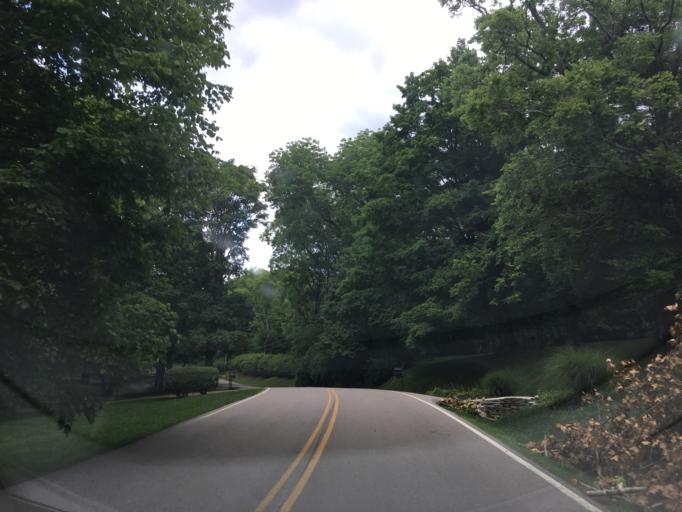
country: US
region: Tennessee
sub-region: Davidson County
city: Forest Hills
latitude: 36.0880
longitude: -86.8277
